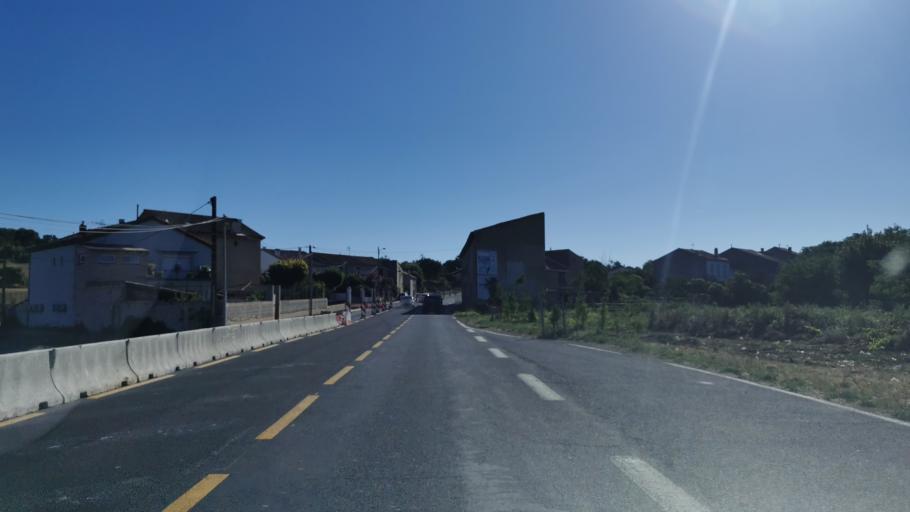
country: FR
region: Languedoc-Roussillon
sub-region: Departement de l'Herault
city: Nissan-lez-Enserune
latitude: 43.2913
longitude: 3.1192
